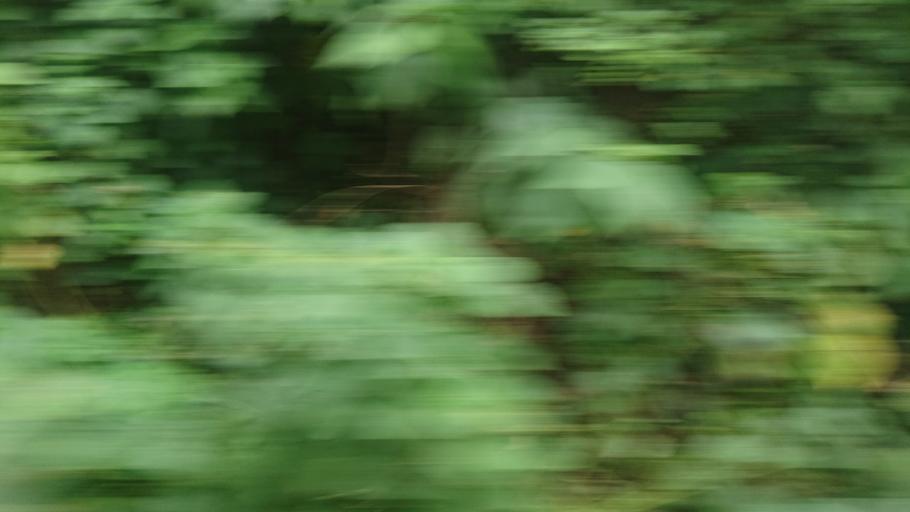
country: TW
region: Taiwan
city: Lugu
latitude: 23.8186
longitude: 120.8452
